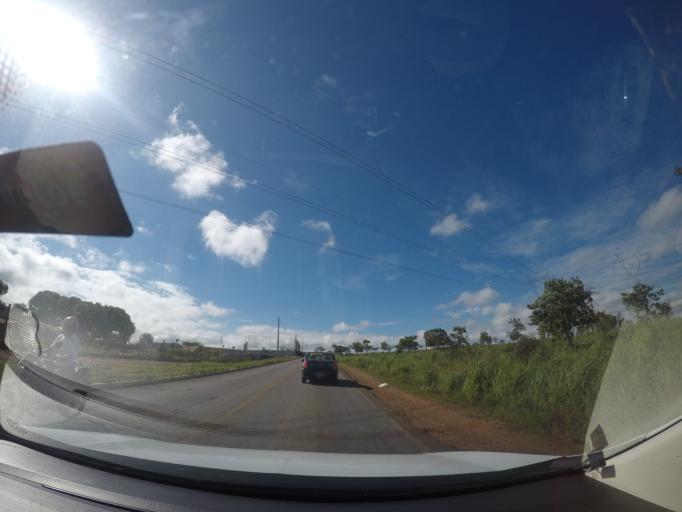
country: BR
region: Goias
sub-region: Senador Canedo
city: Senador Canedo
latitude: -16.6669
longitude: -49.1490
